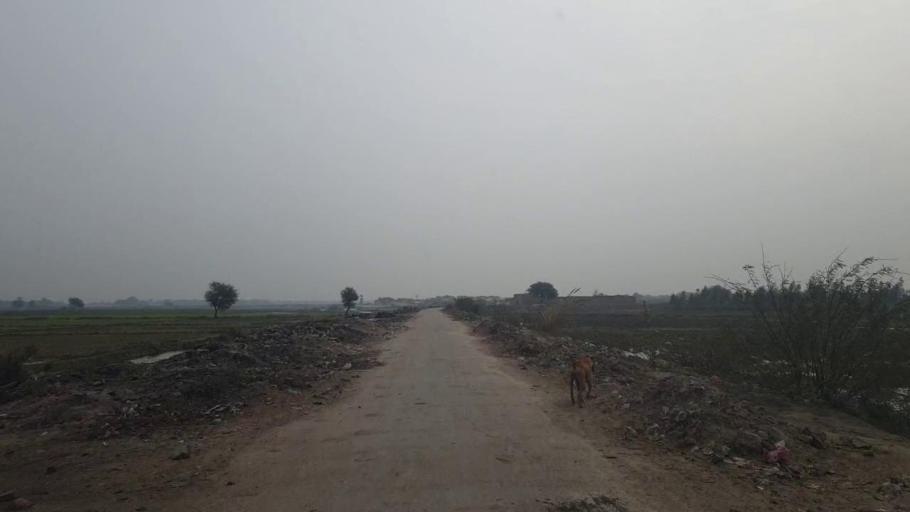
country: PK
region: Sindh
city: Tando Adam
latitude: 25.7528
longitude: 68.6756
